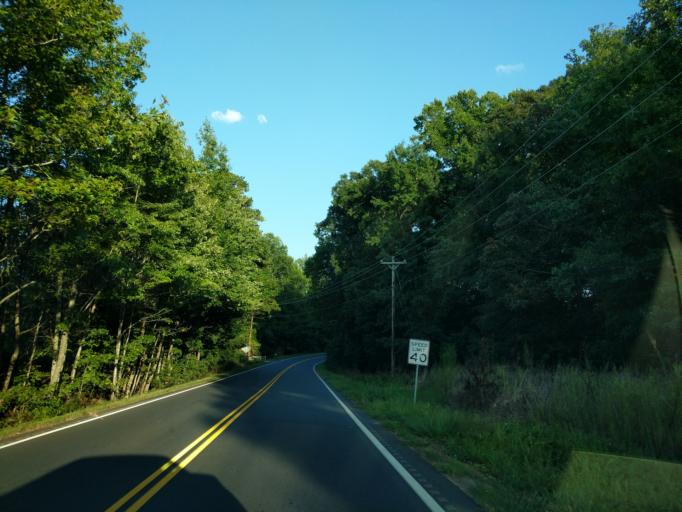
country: US
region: South Carolina
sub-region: Spartanburg County
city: Duncan
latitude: 34.8974
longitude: -82.1459
